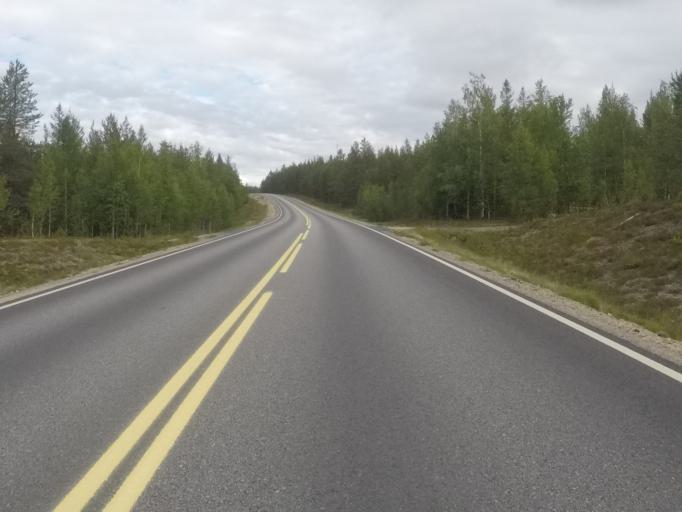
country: FI
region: Lapland
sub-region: Tunturi-Lappi
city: Kolari
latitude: 67.5557
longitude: 23.6072
